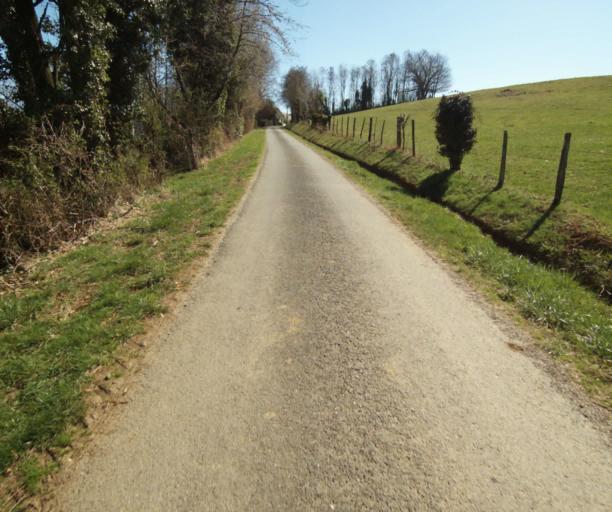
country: FR
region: Limousin
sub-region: Departement de la Correze
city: Saint-Clement
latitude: 45.3854
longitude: 1.6536
